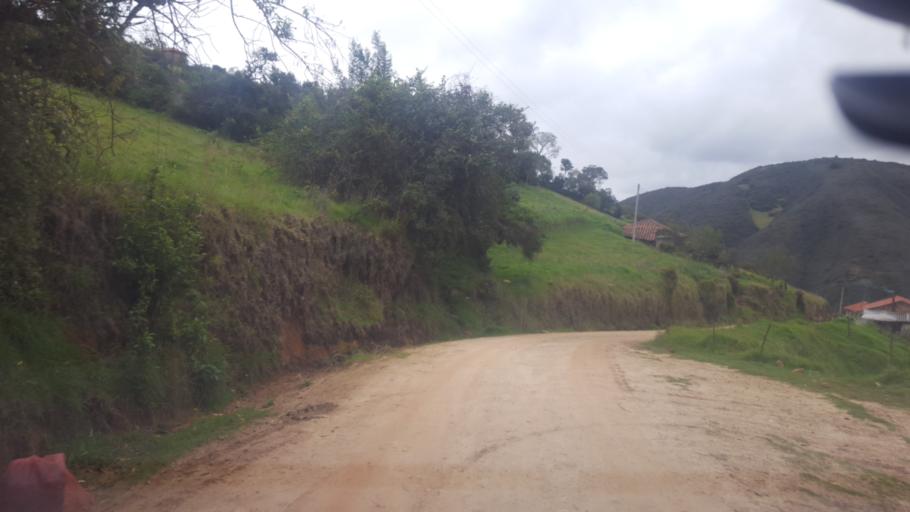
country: CO
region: Boyaca
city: Belen
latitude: 6.0200
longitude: -72.8789
